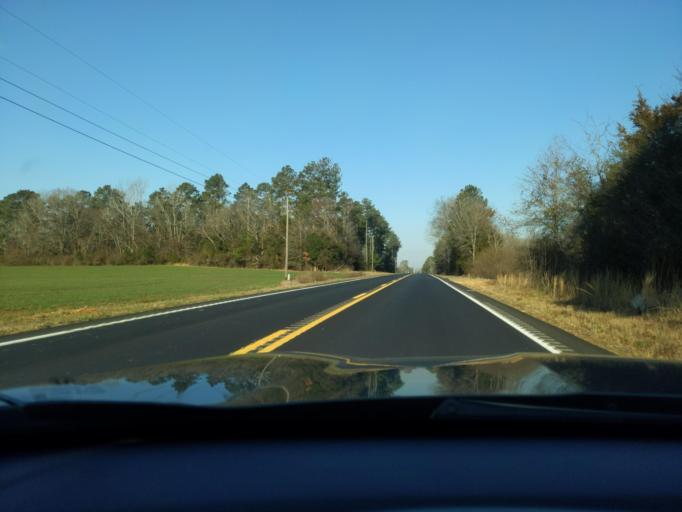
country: US
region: South Carolina
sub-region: Newberry County
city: Newberry
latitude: 34.1985
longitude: -81.8007
